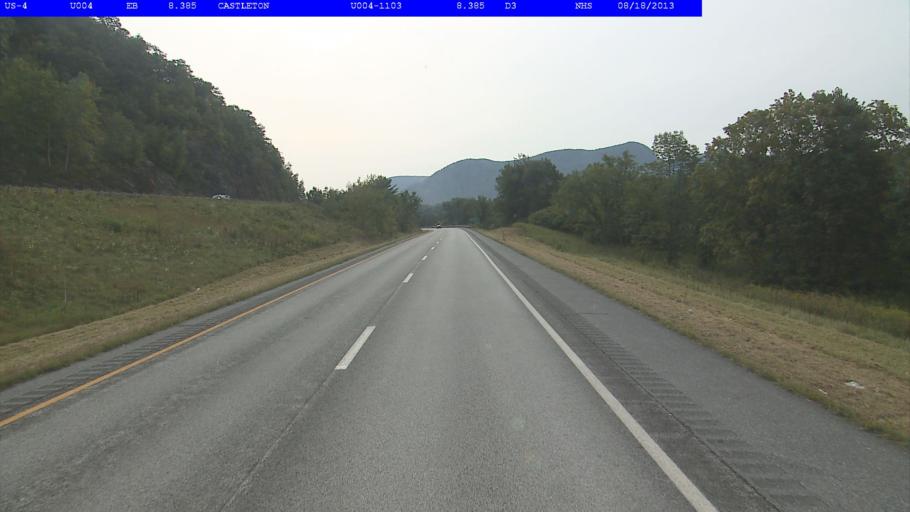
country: US
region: Vermont
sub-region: Rutland County
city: Castleton
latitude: 43.6157
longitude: -73.1538
